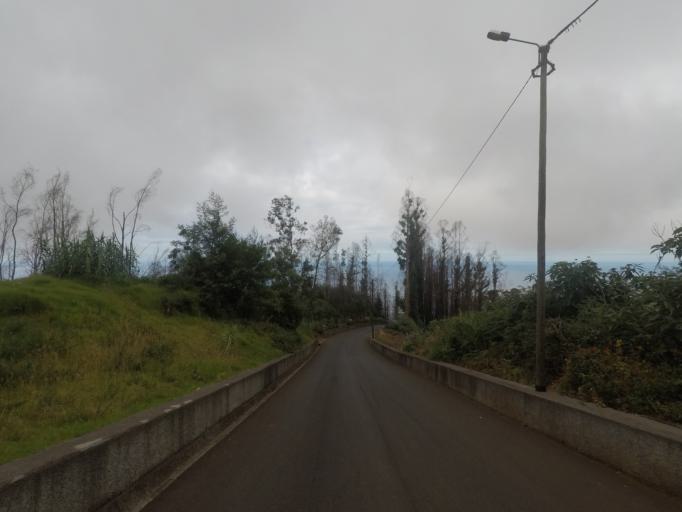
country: PT
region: Madeira
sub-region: Funchal
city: Nossa Senhora do Monte
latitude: 32.6690
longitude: -16.8836
